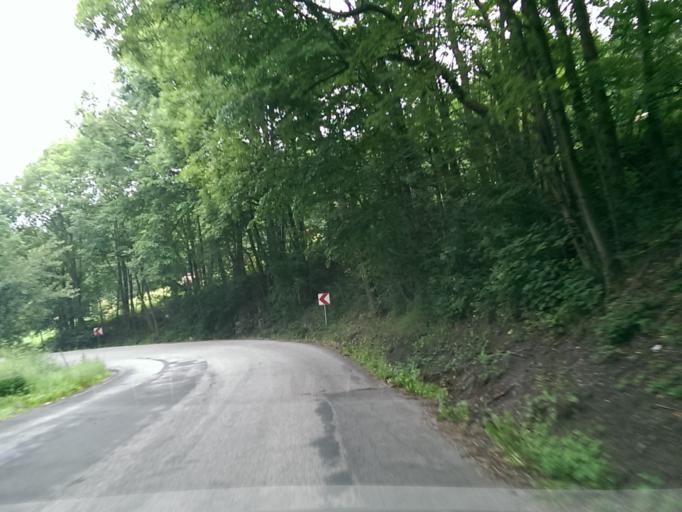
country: CZ
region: Liberecky
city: Rovensko pod Troskami
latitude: 50.5855
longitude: 15.2694
